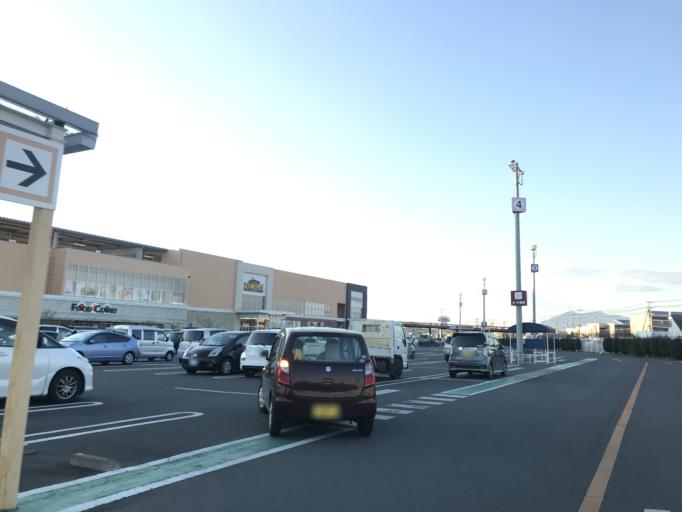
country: JP
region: Ibaraki
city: Naka
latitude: 36.0757
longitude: 140.0717
